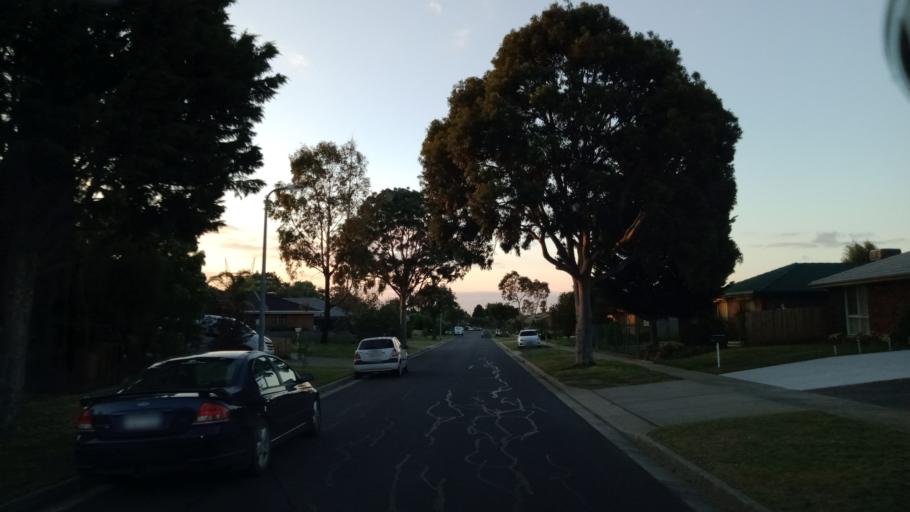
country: AU
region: Victoria
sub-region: Casey
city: Cranbourne North
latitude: -38.0851
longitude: 145.2690
